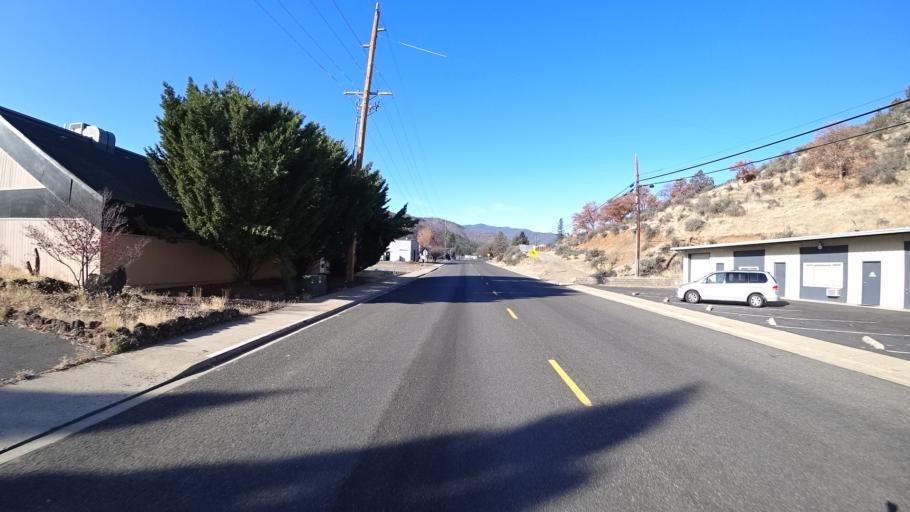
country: US
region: California
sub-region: Siskiyou County
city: Yreka
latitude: 41.7119
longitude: -122.6451
